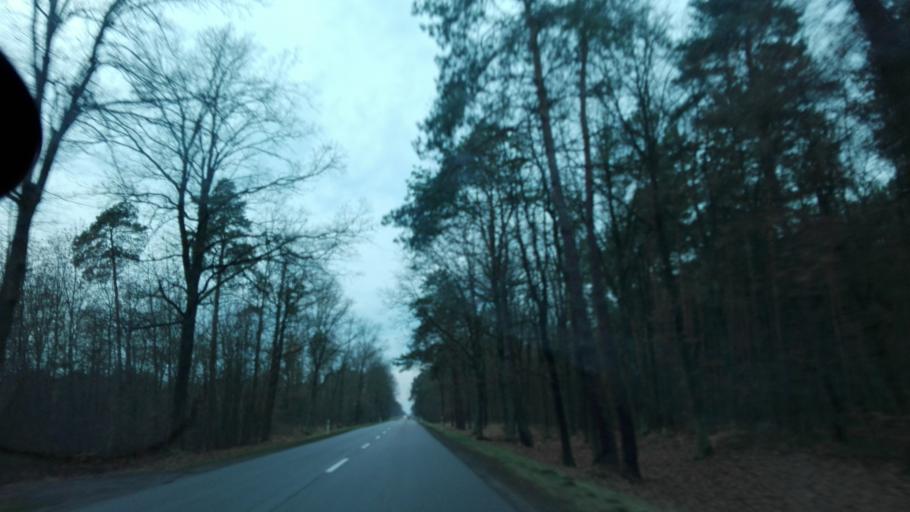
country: PL
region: Lublin Voivodeship
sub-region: Powiat radzynski
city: Radzyn Podlaski
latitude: 51.7773
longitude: 22.6692
